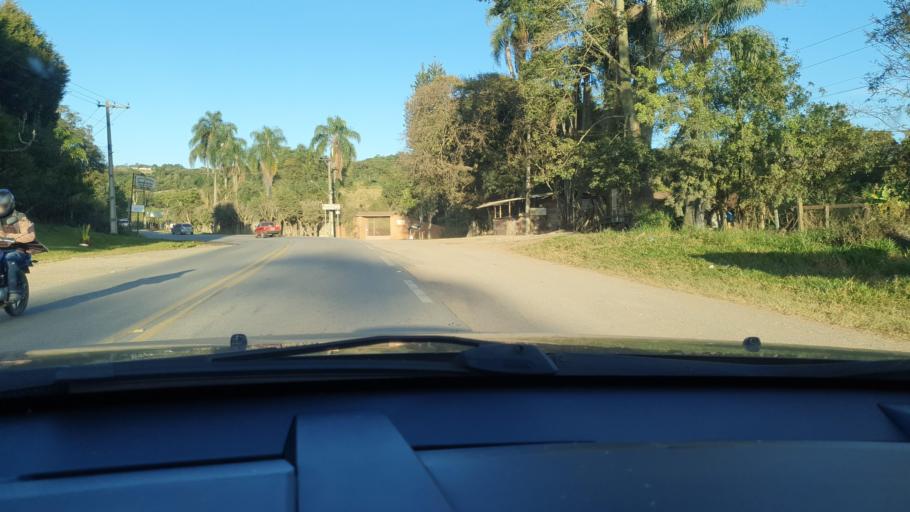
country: BR
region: Sao Paulo
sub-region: Piedade
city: Piedade
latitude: -23.6797
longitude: -47.3399
